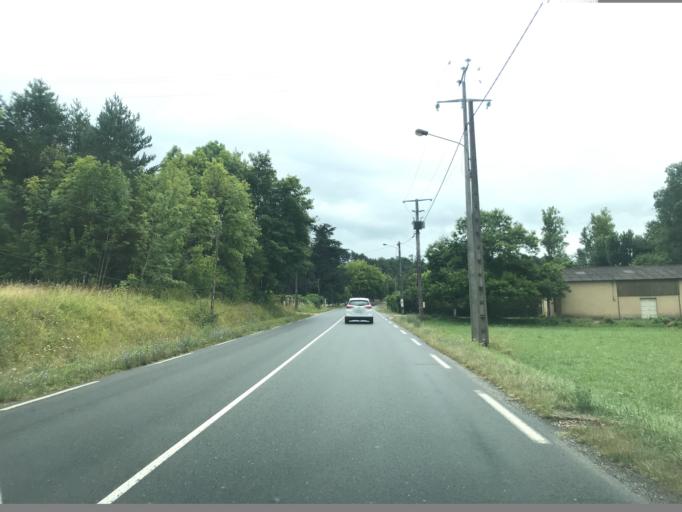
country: FR
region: Aquitaine
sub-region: Departement de la Dordogne
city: Chancelade
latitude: 45.2379
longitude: 0.6853
